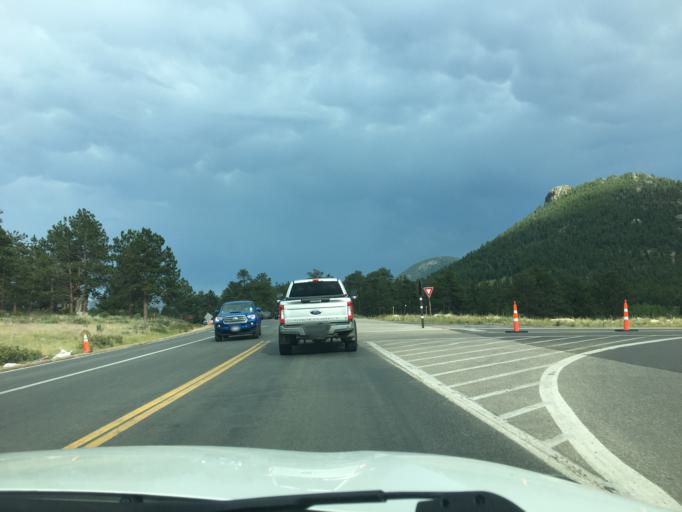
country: US
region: Colorado
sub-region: Larimer County
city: Estes Park
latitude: 40.3659
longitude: -105.5854
